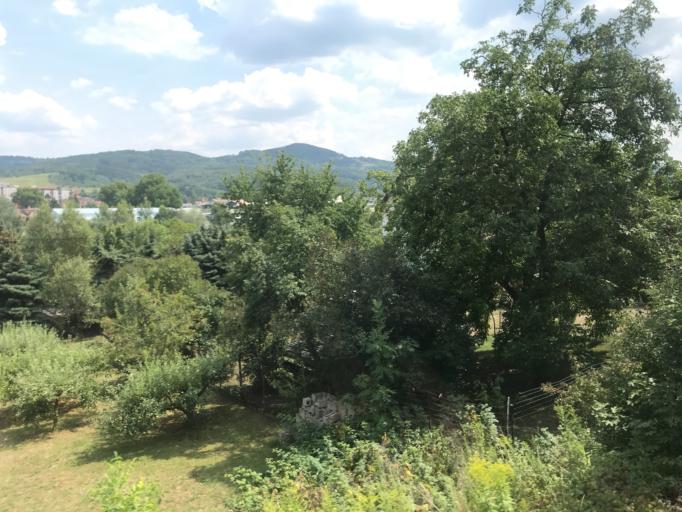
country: CZ
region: Ustecky
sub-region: Okres Decin
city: Decin
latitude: 50.7413
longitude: 14.1801
